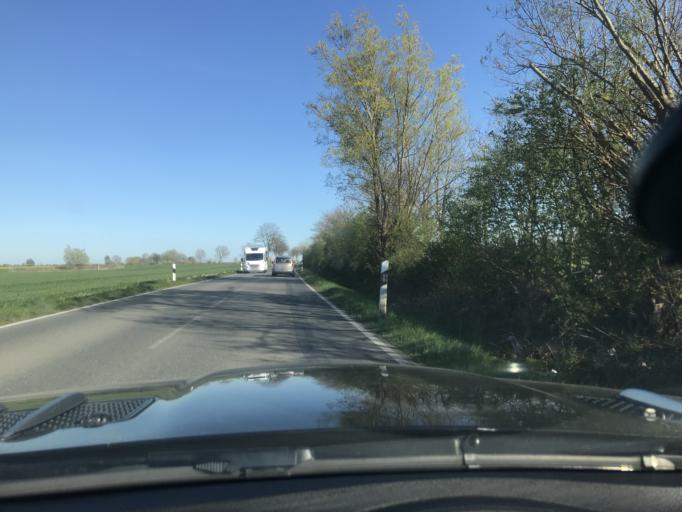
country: DE
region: Schleswig-Holstein
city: Fehmarn
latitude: 54.4662
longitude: 11.1111
